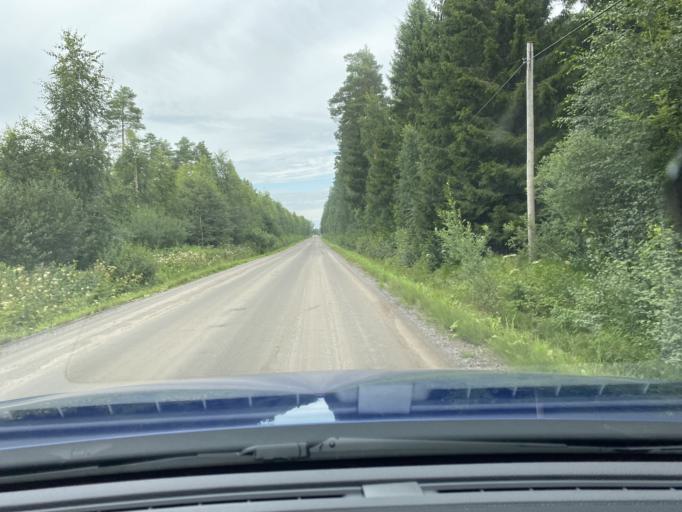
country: FI
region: Satakunta
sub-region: Rauma
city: Kiukainen
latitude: 61.1396
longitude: 21.9937
